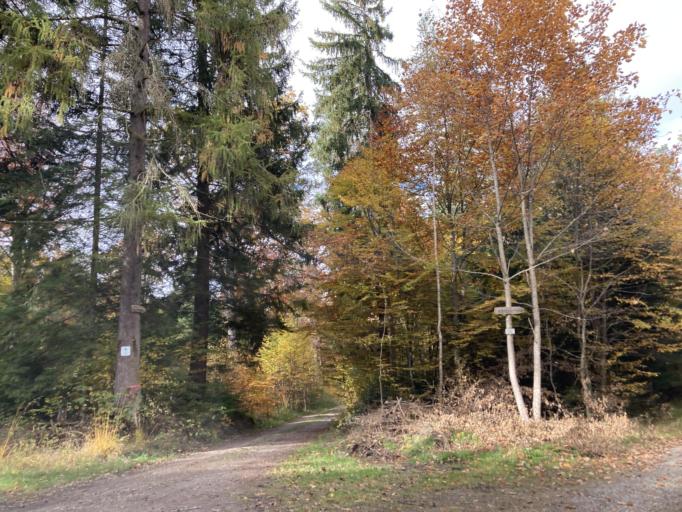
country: DE
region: Baden-Wuerttemberg
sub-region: Tuebingen Region
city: Ofterdingen
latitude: 48.4466
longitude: 8.9932
